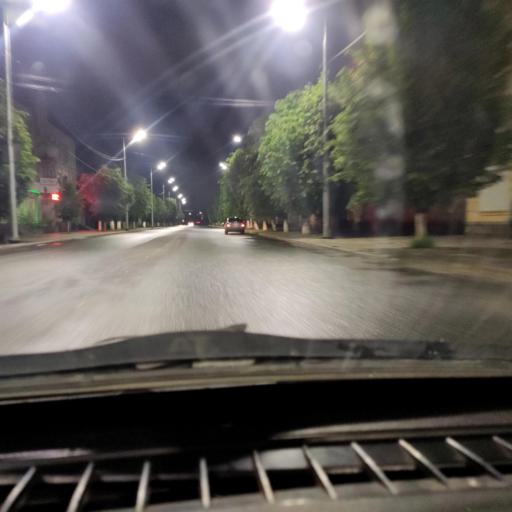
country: RU
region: Samara
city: Syzran'
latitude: 53.1569
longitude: 48.4774
